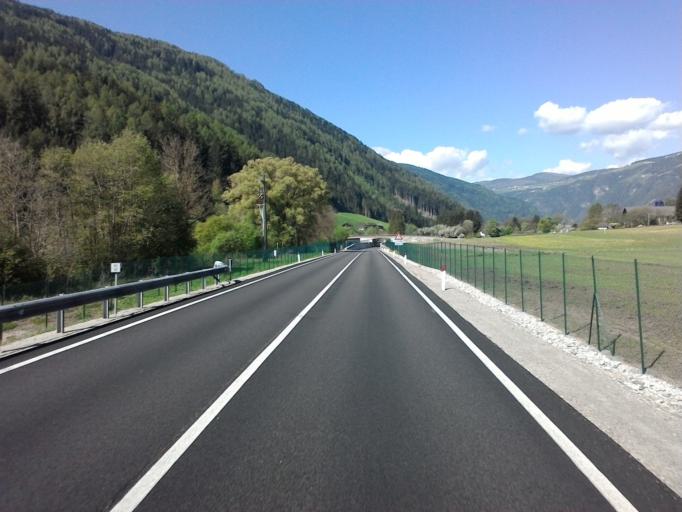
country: IT
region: Trentino-Alto Adige
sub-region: Bolzano
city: Terento
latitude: 46.8099
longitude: 11.7703
